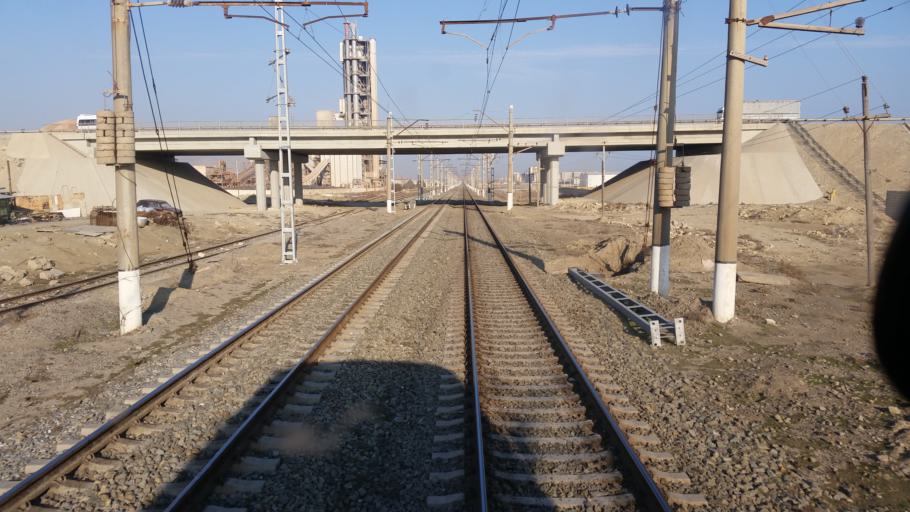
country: AZ
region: Baki
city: Korgoz
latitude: 40.2180
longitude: 49.5499
